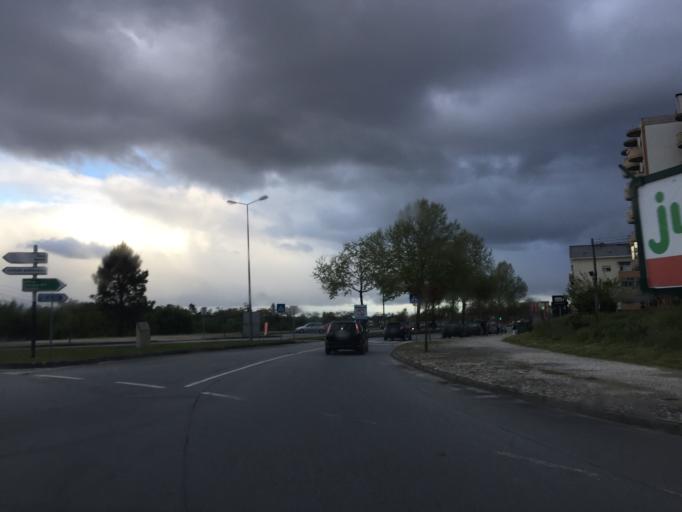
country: PT
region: Viseu
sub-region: Viseu
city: Viseu
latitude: 40.6439
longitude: -7.9240
